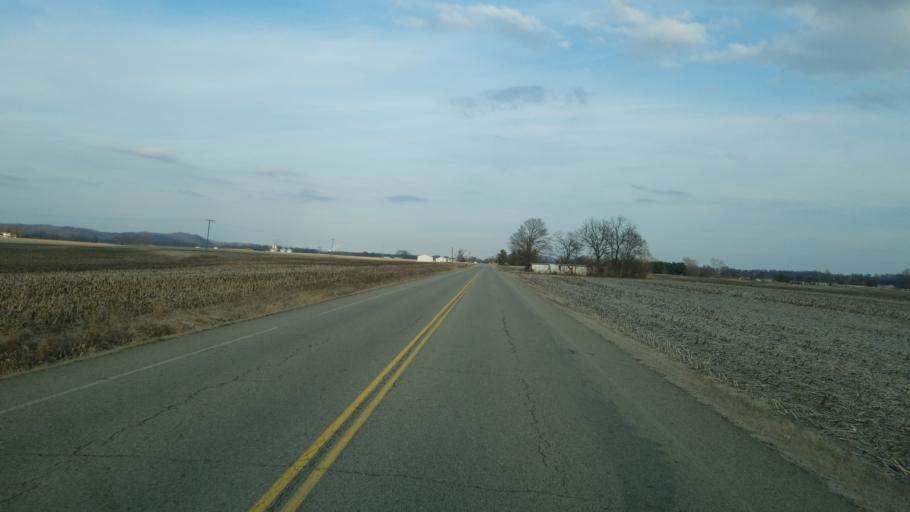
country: US
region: Ohio
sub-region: Ross County
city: Chillicothe
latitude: 39.2429
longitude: -82.8663
